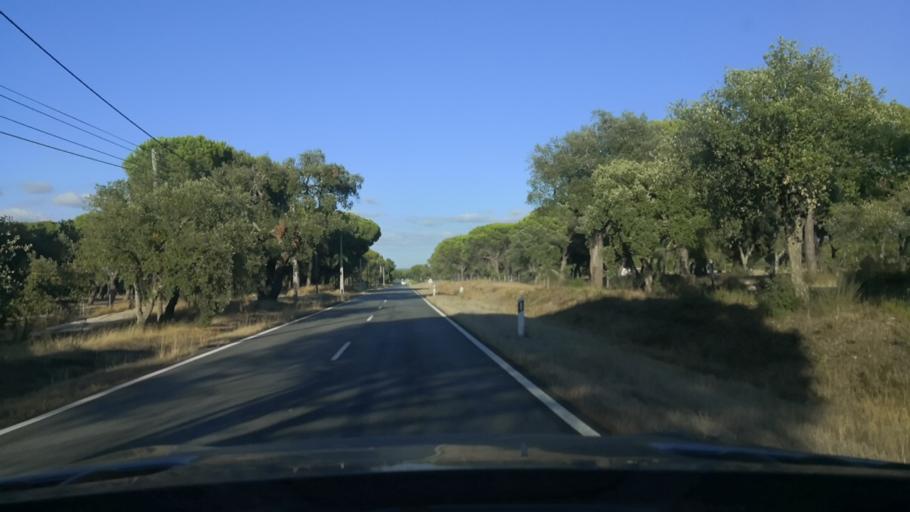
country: PT
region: Setubal
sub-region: Alcacer do Sal
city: Alcacer do Sal
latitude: 38.3949
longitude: -8.6226
